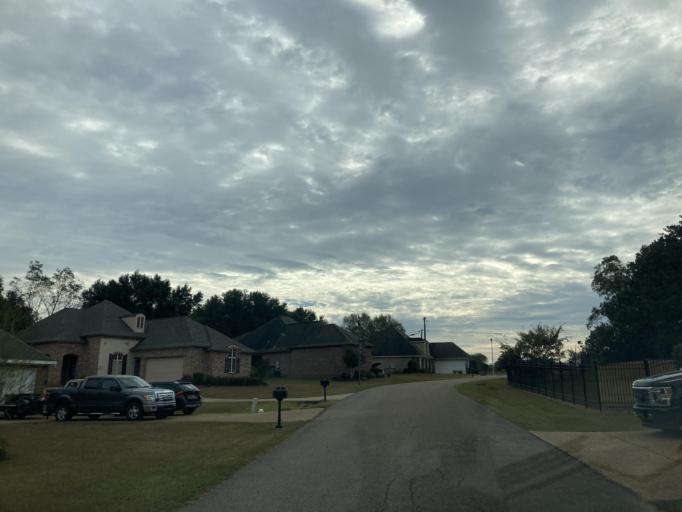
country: US
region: Mississippi
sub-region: Lamar County
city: West Hattiesburg
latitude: 31.2975
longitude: -89.3875
